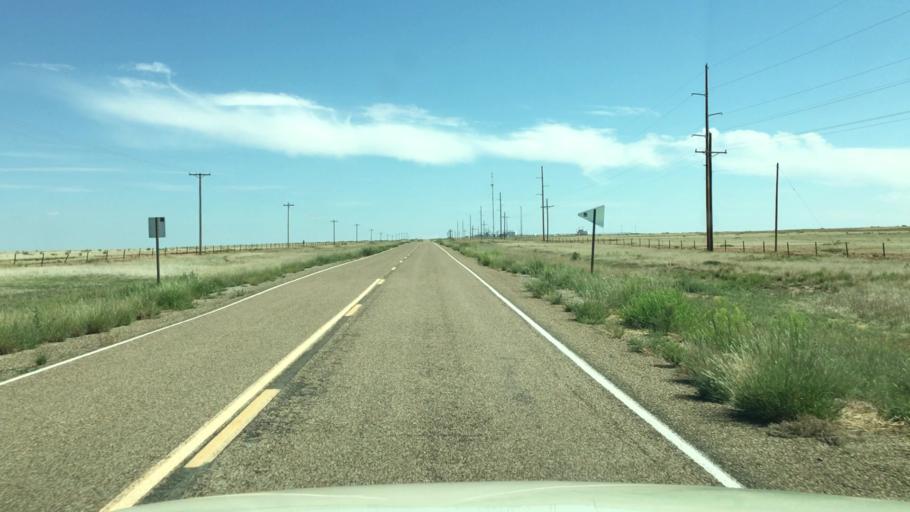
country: US
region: New Mexico
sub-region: Chaves County
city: Roswell
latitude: 33.9546
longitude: -104.5865
